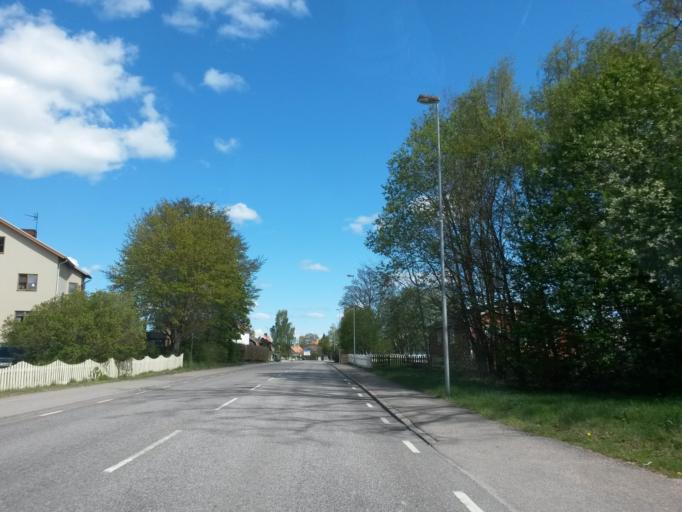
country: SE
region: Vaestra Goetaland
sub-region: Herrljunga Kommun
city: Herrljunga
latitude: 58.0775
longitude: 13.0092
